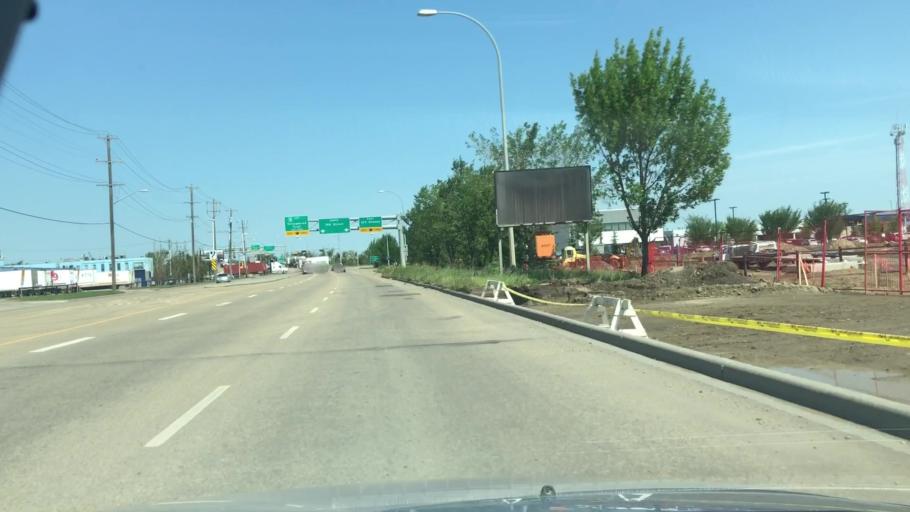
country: CA
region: Alberta
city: St. Albert
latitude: 53.5753
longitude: -113.5904
